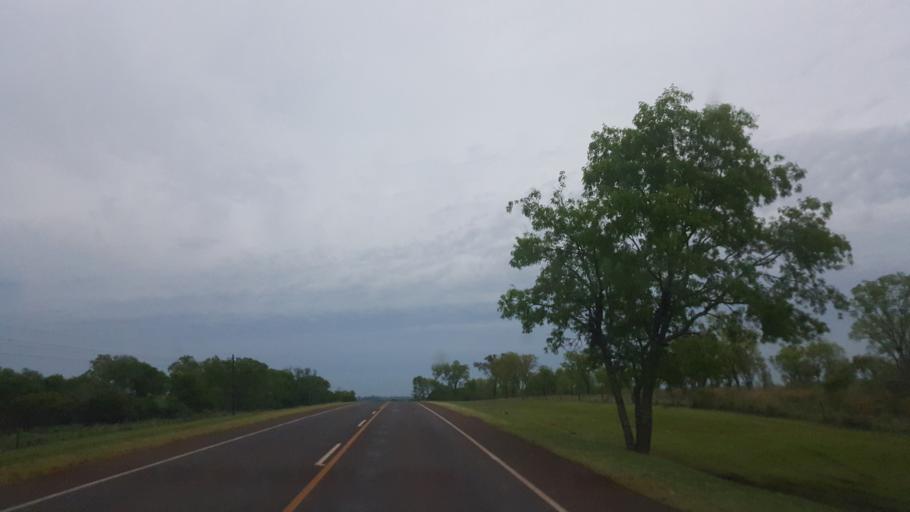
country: AR
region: Misiones
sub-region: Departamento de Apostoles
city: San Jose
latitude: -27.7166
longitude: -55.7939
